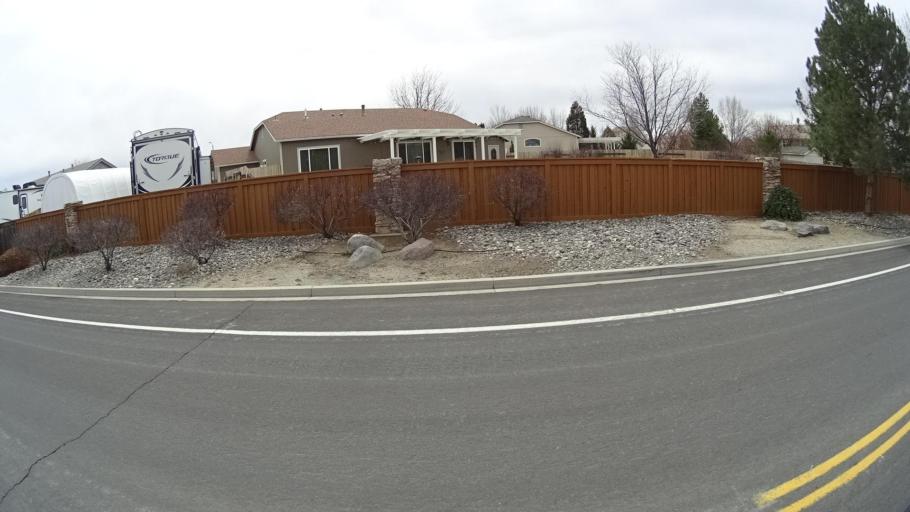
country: US
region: Nevada
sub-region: Washoe County
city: Spanish Springs
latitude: 39.6338
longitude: -119.6900
